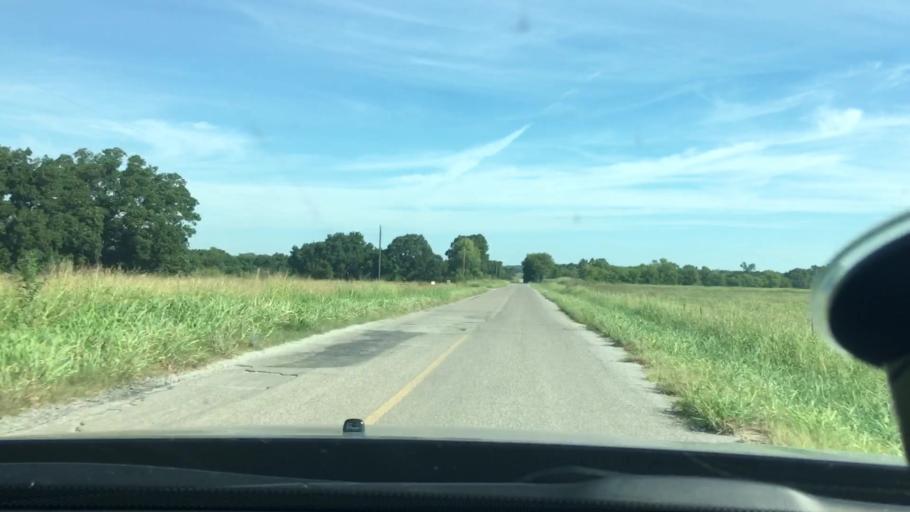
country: US
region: Oklahoma
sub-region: Carter County
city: Lone Grove
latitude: 34.3017
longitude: -97.2819
